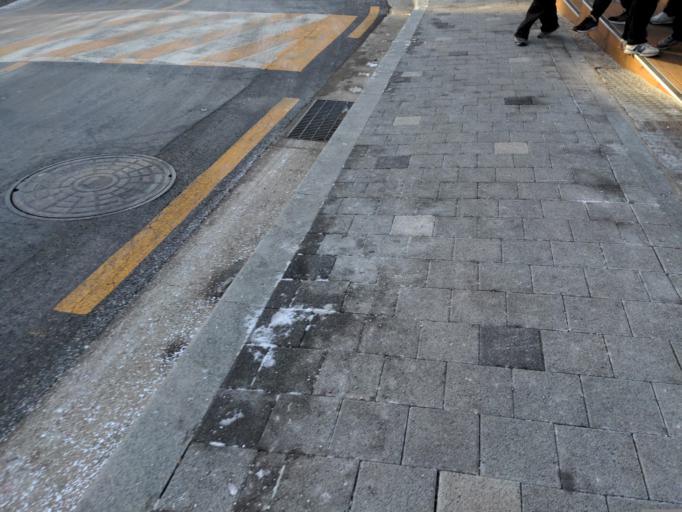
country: KR
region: Seoul
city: Seoul
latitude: 37.5609
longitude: 127.0455
